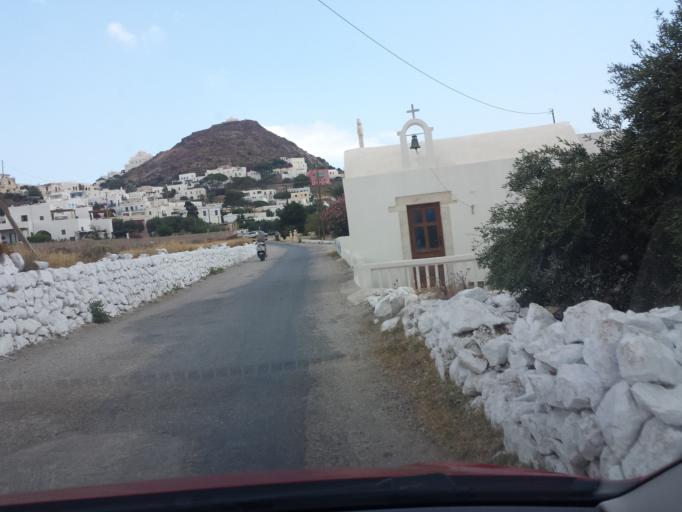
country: GR
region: South Aegean
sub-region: Nomos Kykladon
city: Milos
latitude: 36.7412
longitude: 24.4249
